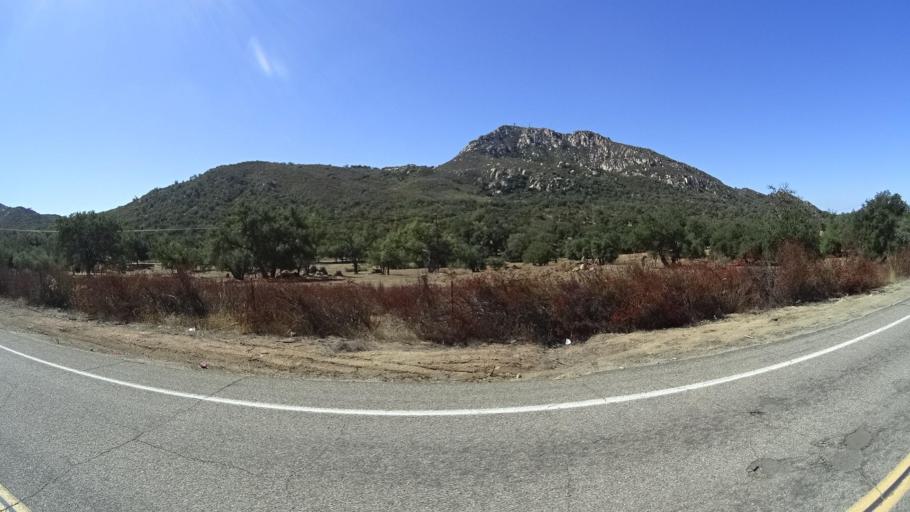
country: US
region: California
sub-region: San Diego County
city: Alpine
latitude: 32.7150
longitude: -116.7513
